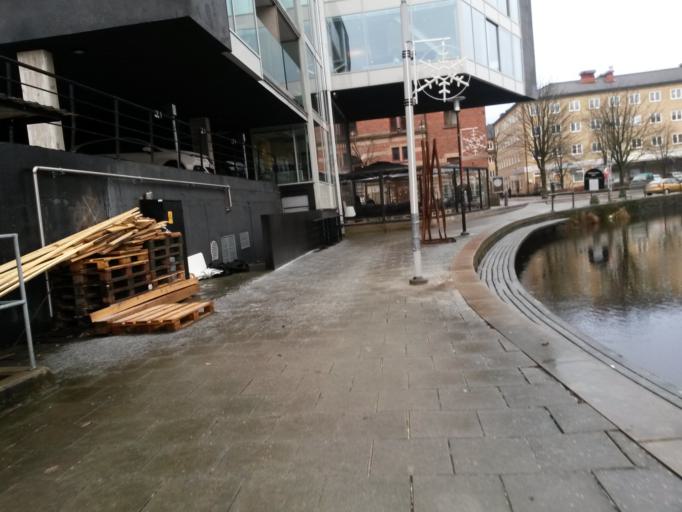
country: SE
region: Vaestra Goetaland
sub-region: Boras Kommun
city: Boras
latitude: 57.7221
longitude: 12.9376
